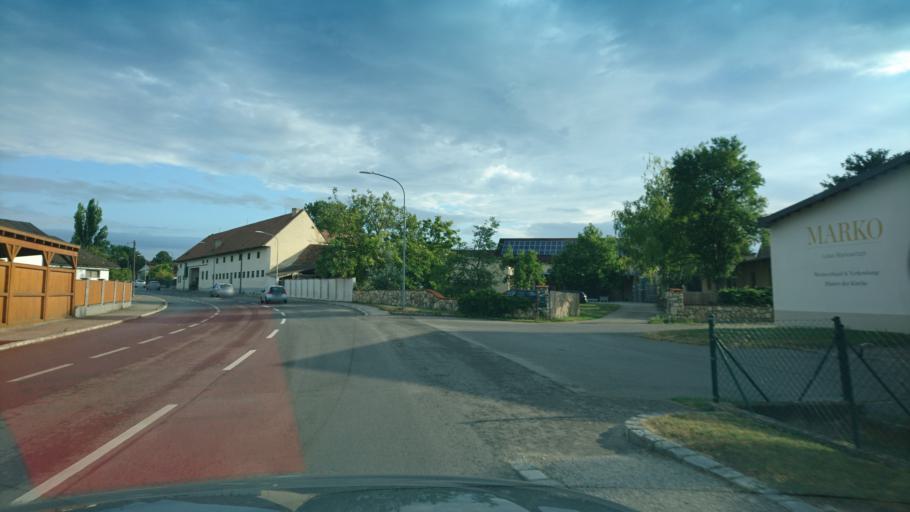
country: AT
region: Lower Austria
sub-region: Politischer Bezirk Bruck an der Leitha
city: Bruck an der Leitha
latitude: 48.0559
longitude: 16.7365
